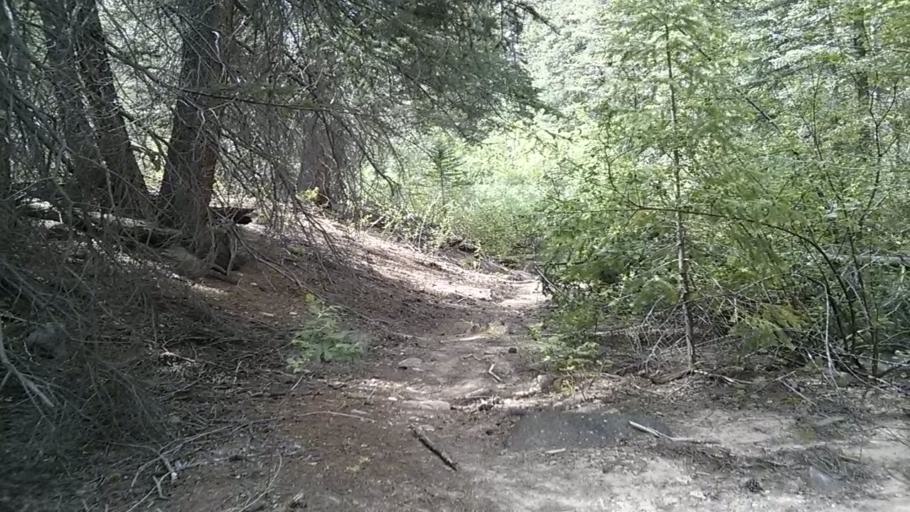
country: US
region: Utah
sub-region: Wayne County
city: Loa
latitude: 37.9576
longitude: -111.6508
